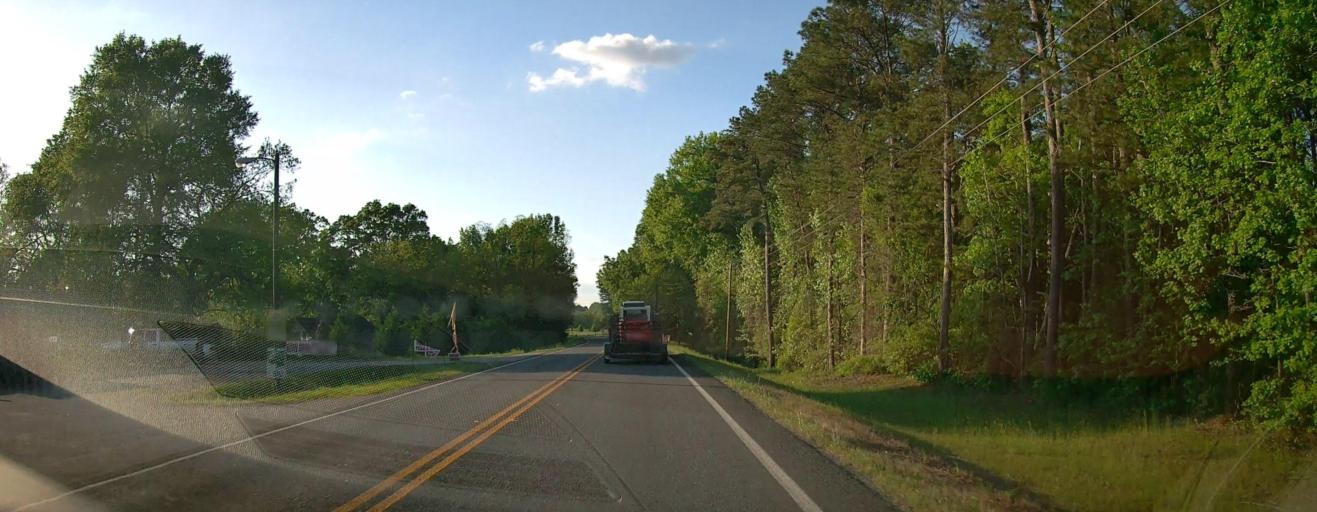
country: US
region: Georgia
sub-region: Jasper County
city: Monticello
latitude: 33.4599
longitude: -83.6328
